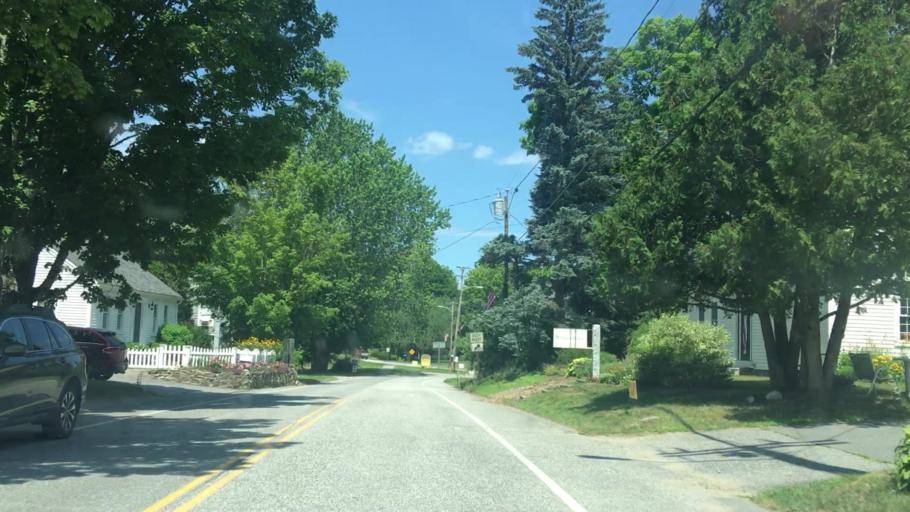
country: US
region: Maine
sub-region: Kennebec County
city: Wayne
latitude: 44.3473
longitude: -70.0657
